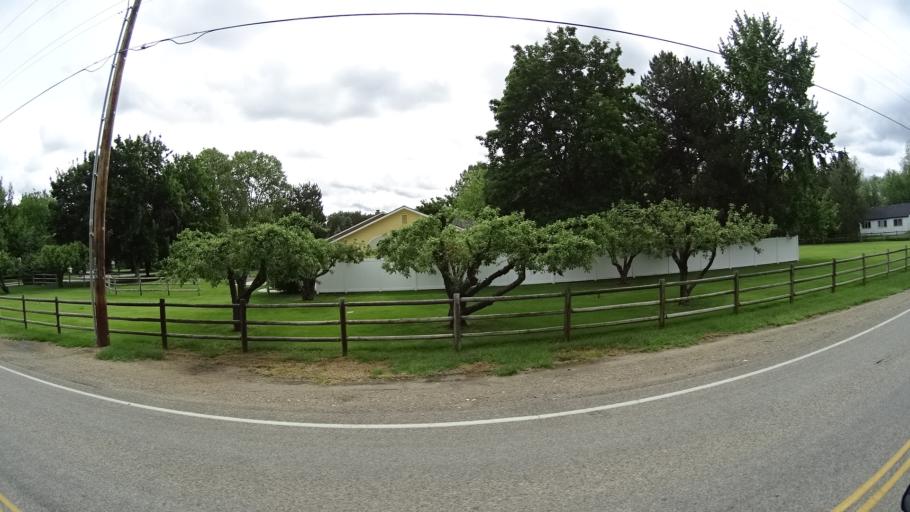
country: US
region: Idaho
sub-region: Ada County
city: Eagle
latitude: 43.7107
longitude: -116.3540
